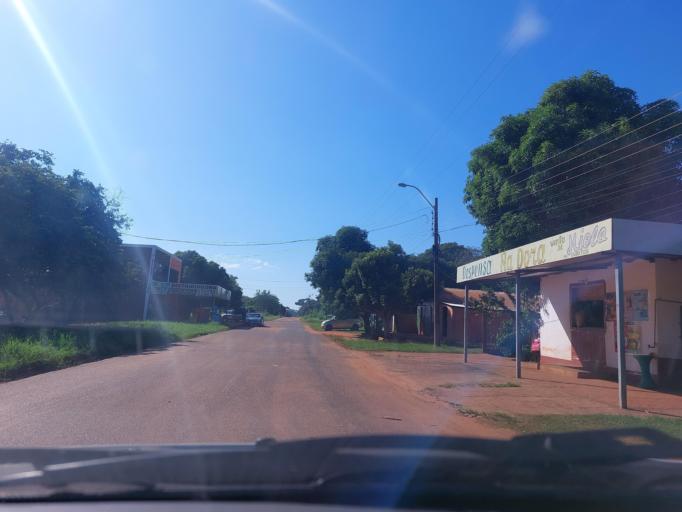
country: PY
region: San Pedro
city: Guayaybi
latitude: -24.5309
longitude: -56.4007
